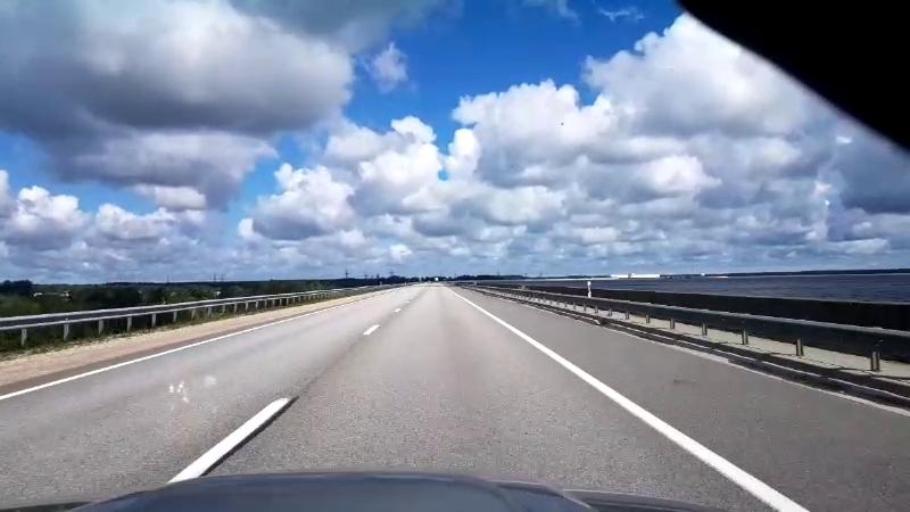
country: LV
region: Kekava
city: Kekava
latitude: 56.8313
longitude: 24.2716
